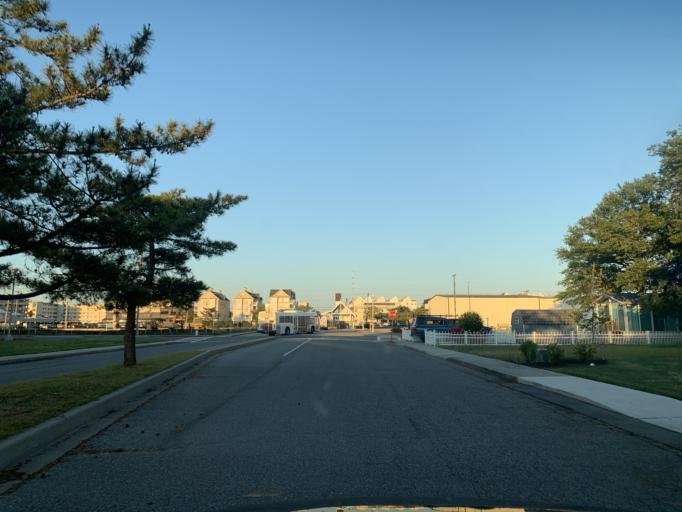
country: US
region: Delaware
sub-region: Sussex County
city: Bethany Beach
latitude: 38.4495
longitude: -75.0548
